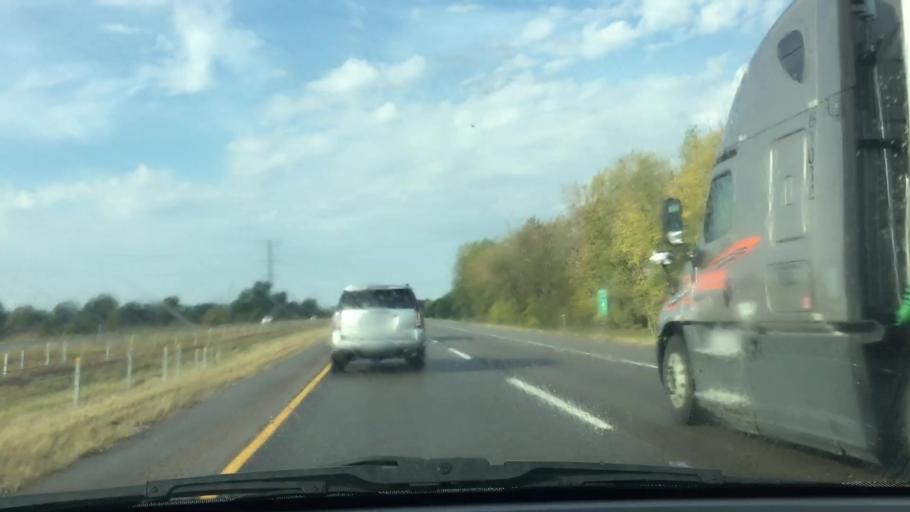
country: US
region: Illinois
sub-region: Whiteside County
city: Rock Falls
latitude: 41.7716
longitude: -89.5881
